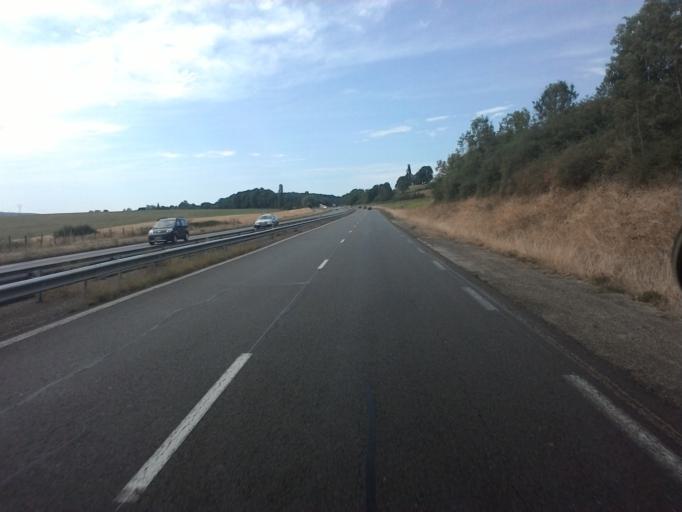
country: FR
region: Franche-Comte
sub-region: Departement du Jura
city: Lons-le-Saunier
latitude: 46.7280
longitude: 5.5579
